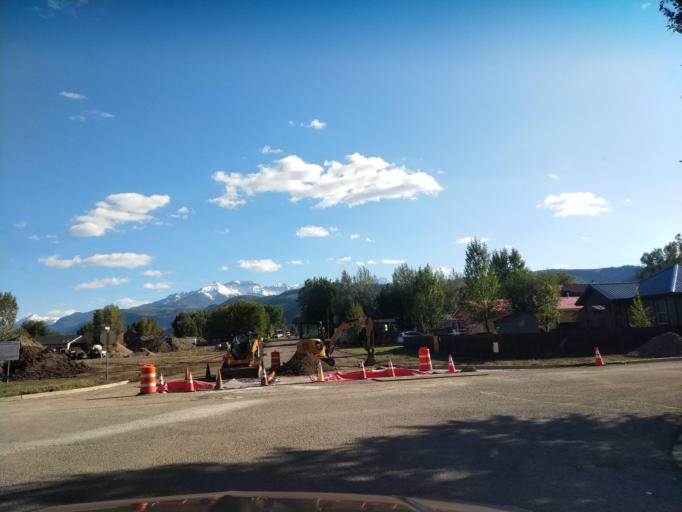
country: US
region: Colorado
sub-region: Ouray County
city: Ouray
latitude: 38.1556
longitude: -107.7562
